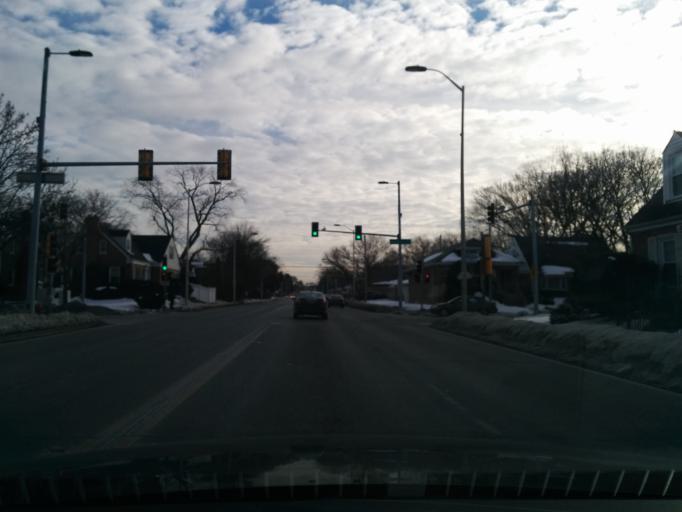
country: US
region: Illinois
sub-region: Cook County
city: Bellwood
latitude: 41.8866
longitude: -87.8790
